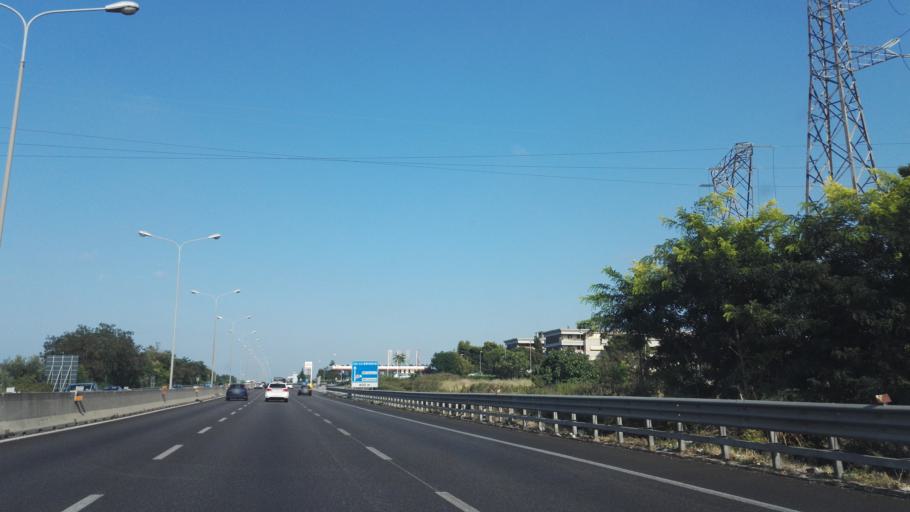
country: IT
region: Apulia
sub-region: Provincia di Bari
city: Bari
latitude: 41.0898
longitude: 16.8601
